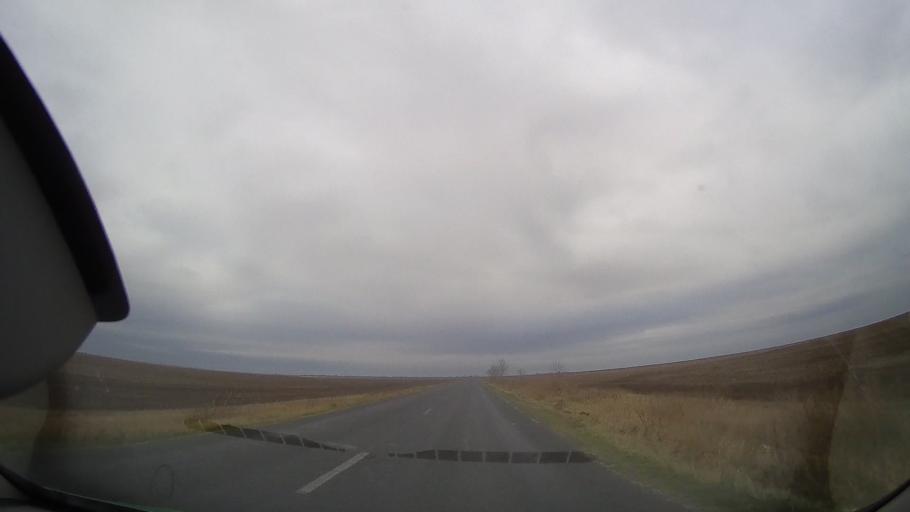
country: RO
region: Buzau
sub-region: Comuna Padina
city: Padina
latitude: 44.8104
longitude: 27.1272
